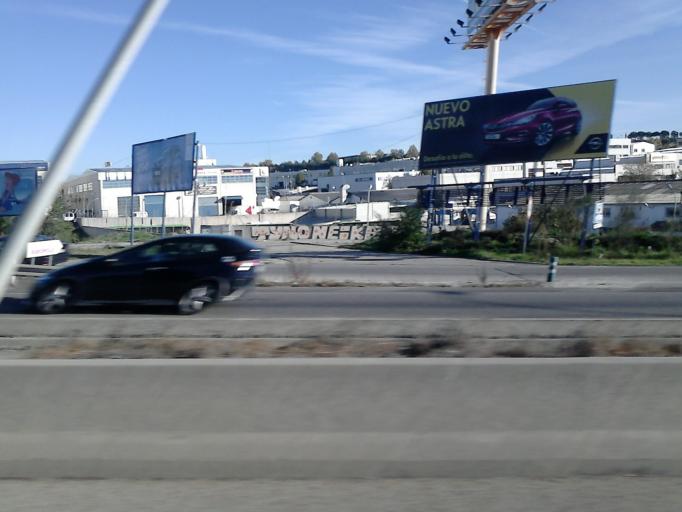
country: ES
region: Madrid
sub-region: Provincia de Madrid
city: Las Rozas de Madrid
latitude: 40.4964
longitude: -3.8888
